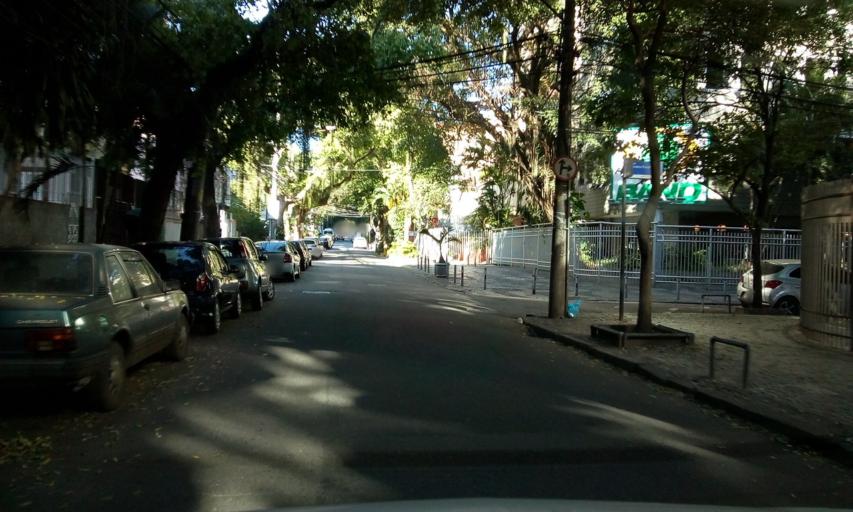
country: BR
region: Rio de Janeiro
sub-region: Rio De Janeiro
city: Rio de Janeiro
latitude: -22.9570
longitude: -43.1830
